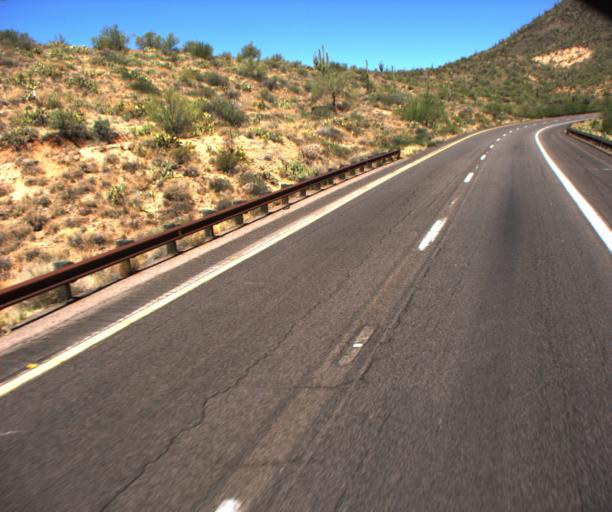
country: US
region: Arizona
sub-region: Gila County
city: Tonto Basin
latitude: 33.8070
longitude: -111.4872
